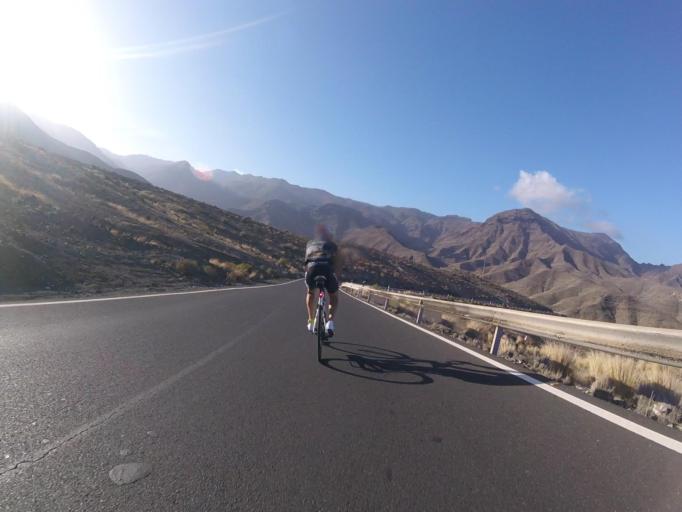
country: ES
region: Canary Islands
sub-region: Provincia de Las Palmas
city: Agaete
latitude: 28.0557
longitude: -15.7316
